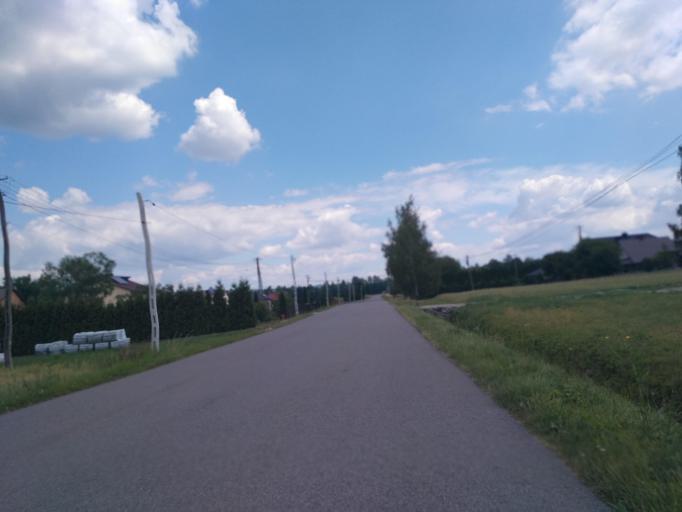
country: PL
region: Subcarpathian Voivodeship
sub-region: Powiat debicki
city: Brzostek
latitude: 49.8589
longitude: 21.4259
